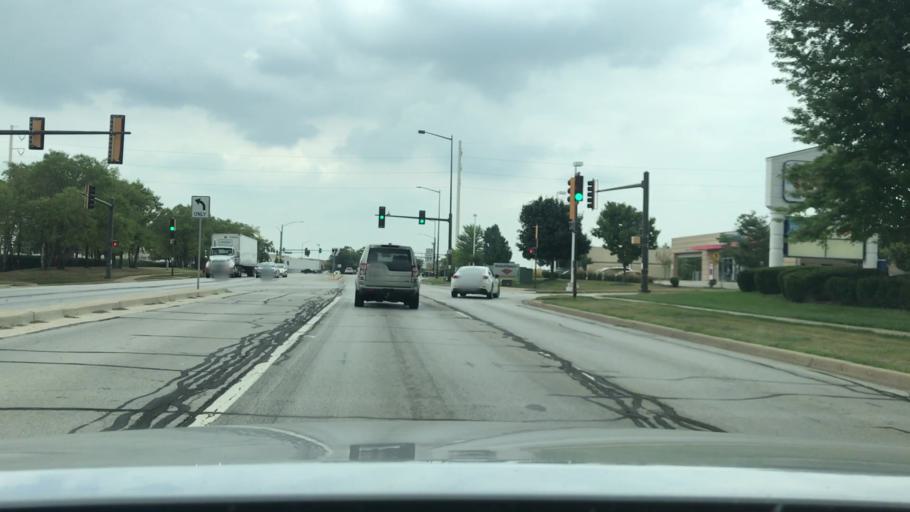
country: US
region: Illinois
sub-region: DuPage County
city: Warrenville
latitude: 41.7699
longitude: -88.2087
